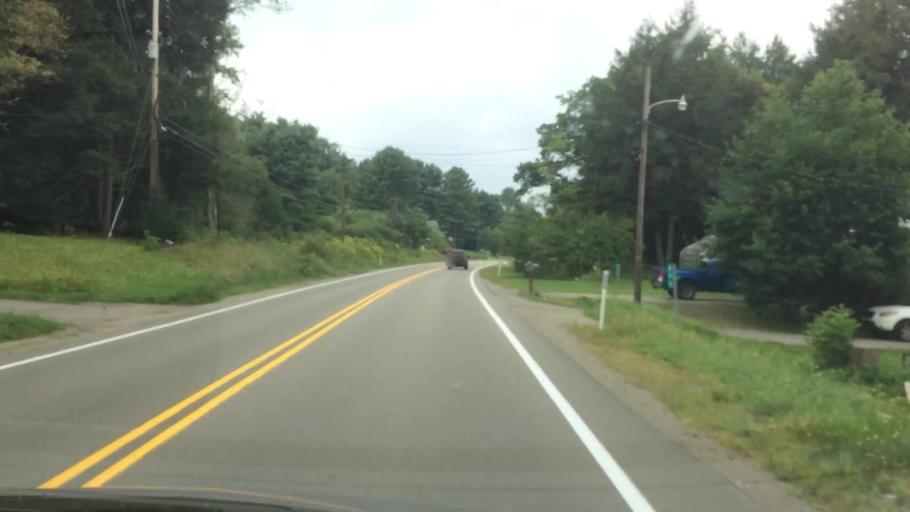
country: US
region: Pennsylvania
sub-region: McKean County
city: Bradford
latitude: 41.8919
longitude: -78.6046
